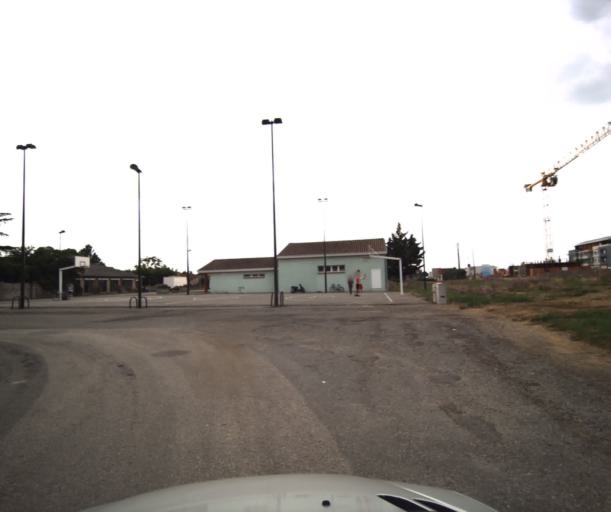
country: FR
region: Midi-Pyrenees
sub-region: Departement de la Haute-Garonne
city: Labarthe-sur-Leze
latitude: 43.4540
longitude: 1.3954
